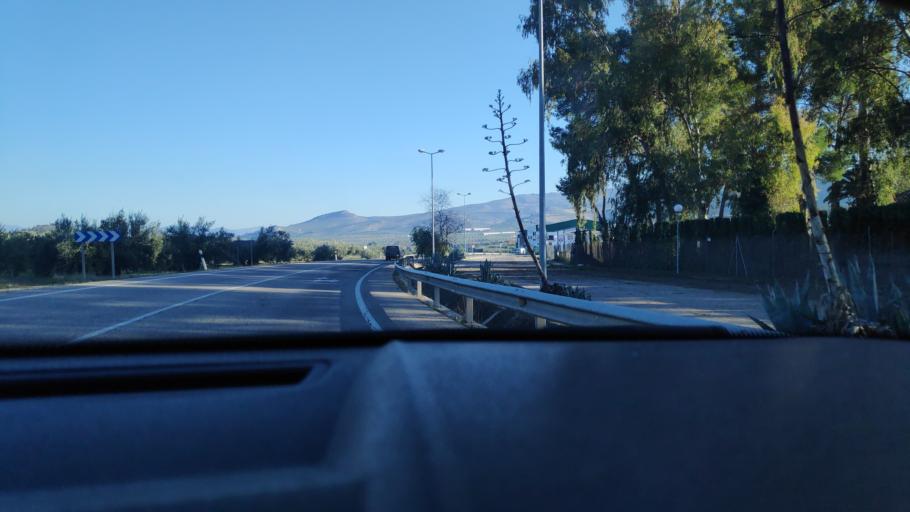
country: ES
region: Andalusia
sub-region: Province of Cordoba
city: Luque
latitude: 37.5723
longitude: -4.2544
